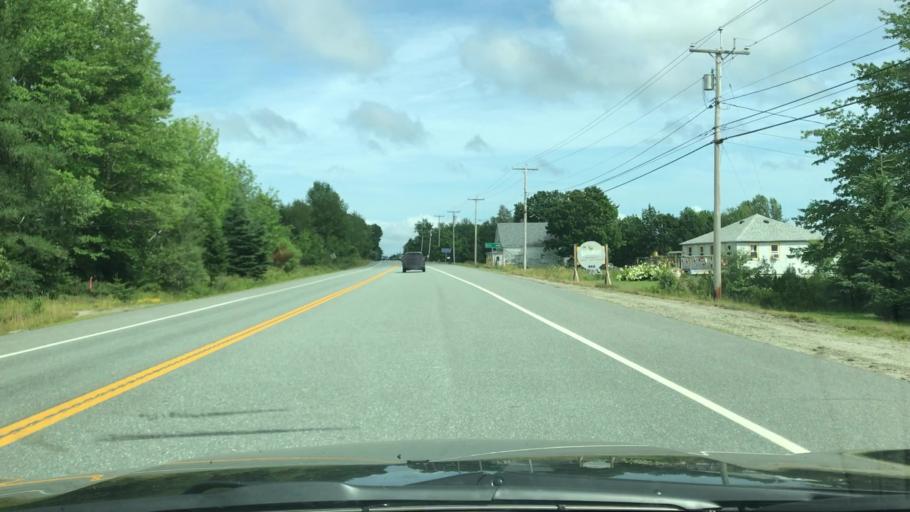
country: US
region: Maine
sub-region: Hancock County
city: Surry
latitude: 44.5457
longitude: -68.5194
